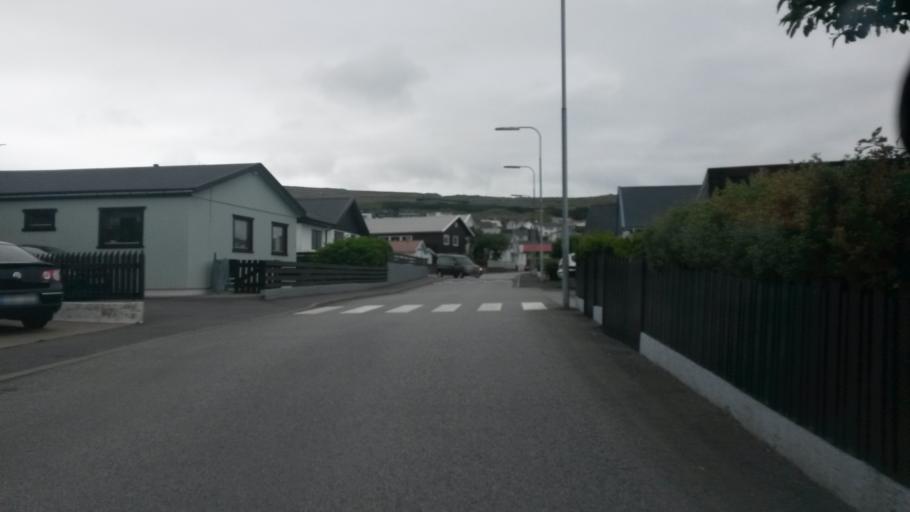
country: FO
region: Streymoy
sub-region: Torshavn
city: Torshavn
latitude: 62.0064
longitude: -6.7897
